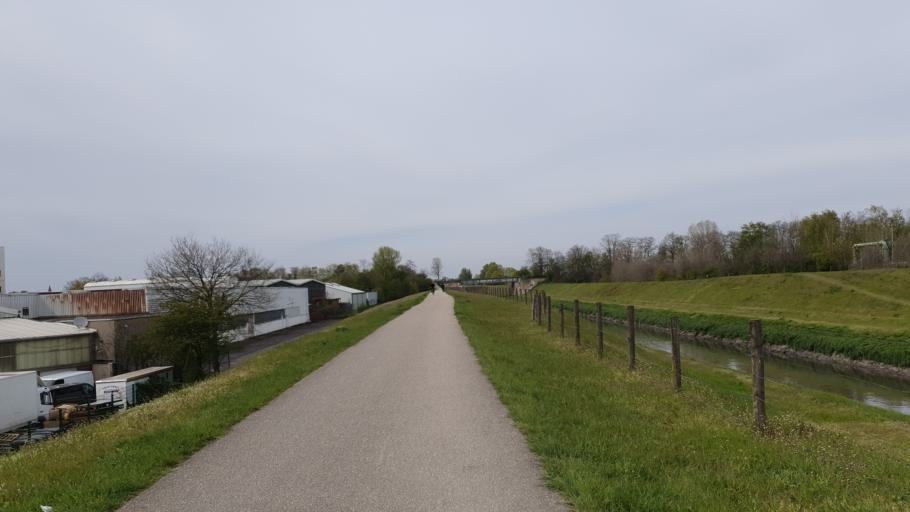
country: DE
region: North Rhine-Westphalia
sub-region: Regierungsbezirk Dusseldorf
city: Oberhausen
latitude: 51.4967
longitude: 6.8449
